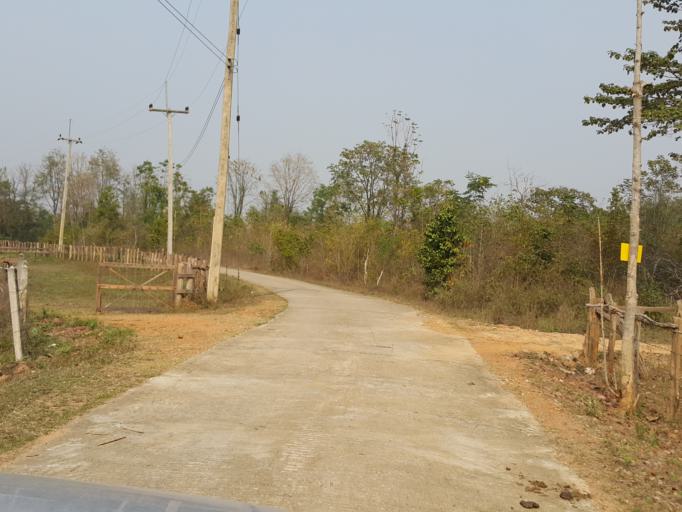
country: TH
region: Lampang
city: Mae Phrik
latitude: 17.4889
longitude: 99.0888
